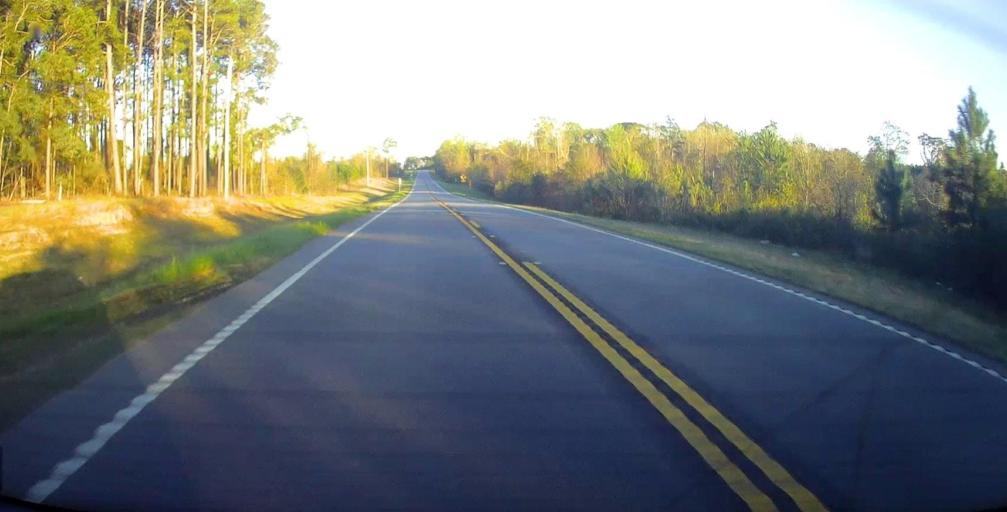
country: US
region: Georgia
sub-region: Crisp County
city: Cordele
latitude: 31.9535
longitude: -83.7223
